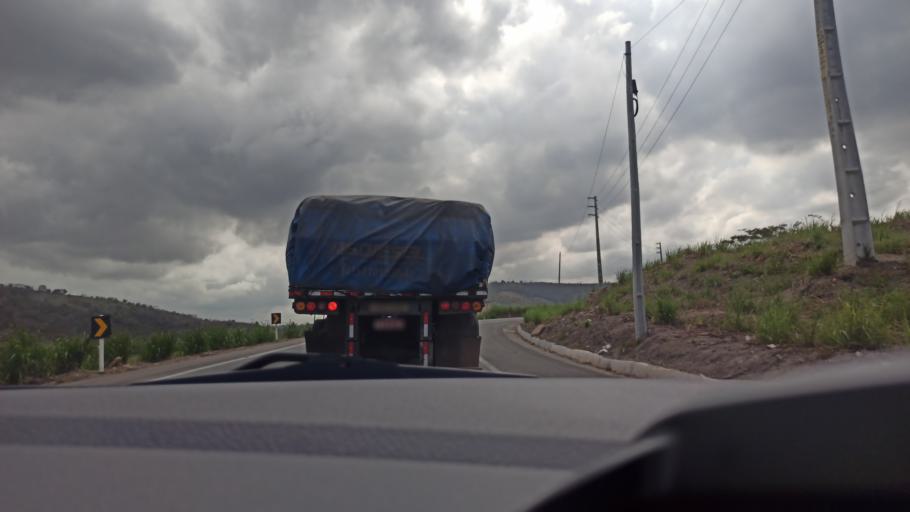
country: BR
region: Pernambuco
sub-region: Timbauba
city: Timbauba
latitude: -7.5227
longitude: -35.2943
